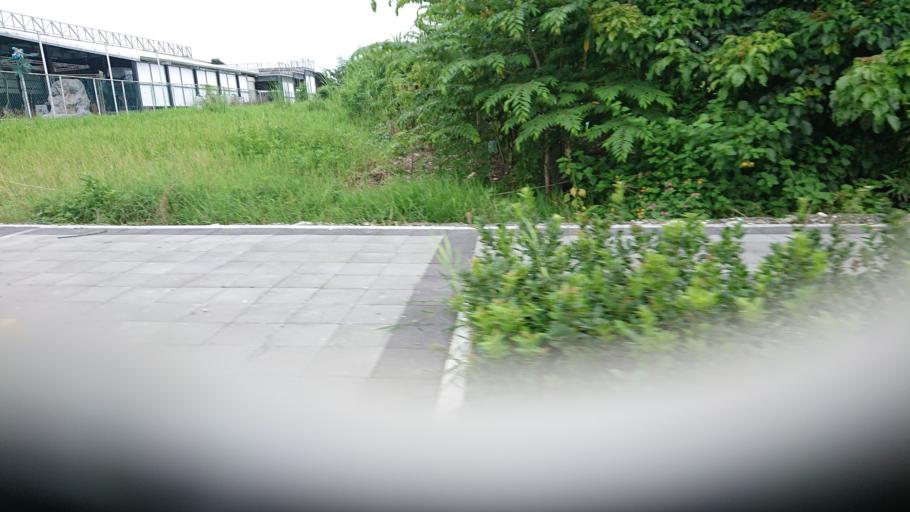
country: TW
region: Taiwan
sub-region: Hualien
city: Hualian
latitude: 23.9623
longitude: 121.6048
